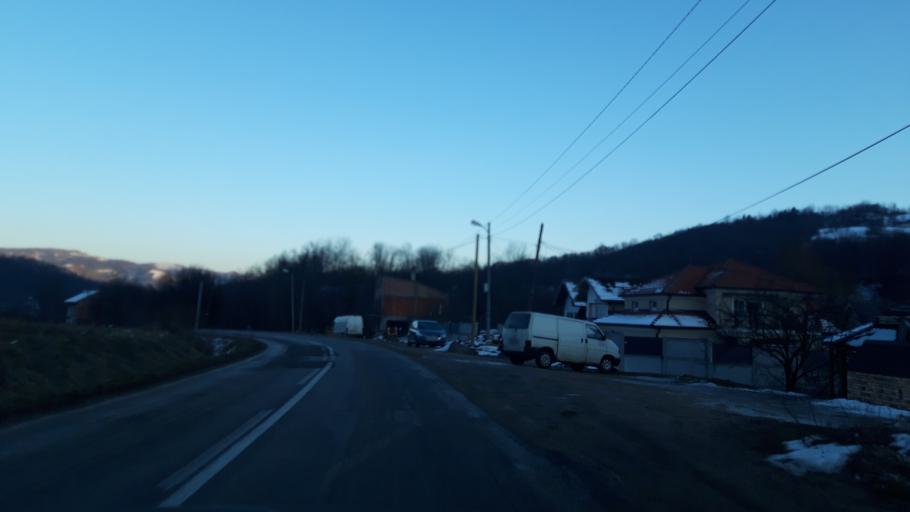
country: BA
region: Republika Srpska
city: Milici
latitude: 44.1639
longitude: 19.0471
